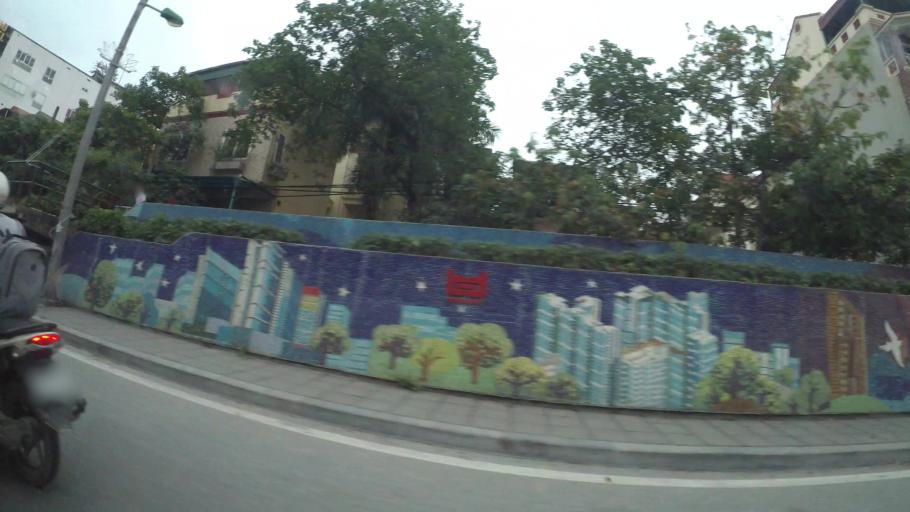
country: VN
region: Ha Noi
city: Hoan Kiem
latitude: 21.0214
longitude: 105.8617
